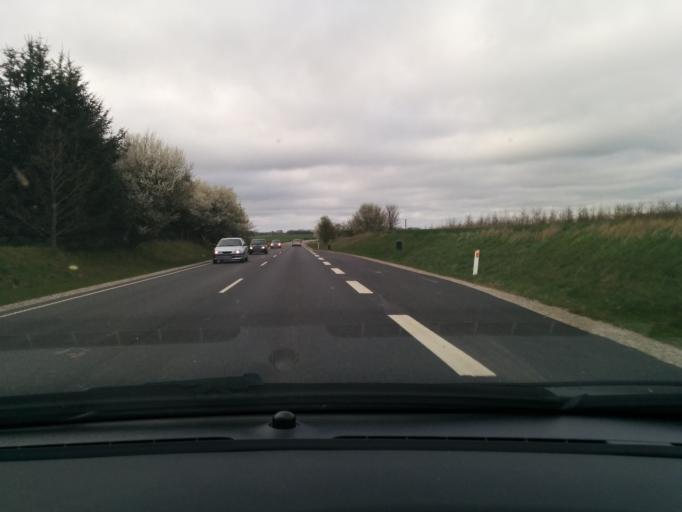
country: DK
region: Central Jutland
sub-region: Favrskov Kommune
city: Hammel
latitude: 56.2192
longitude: 9.8503
